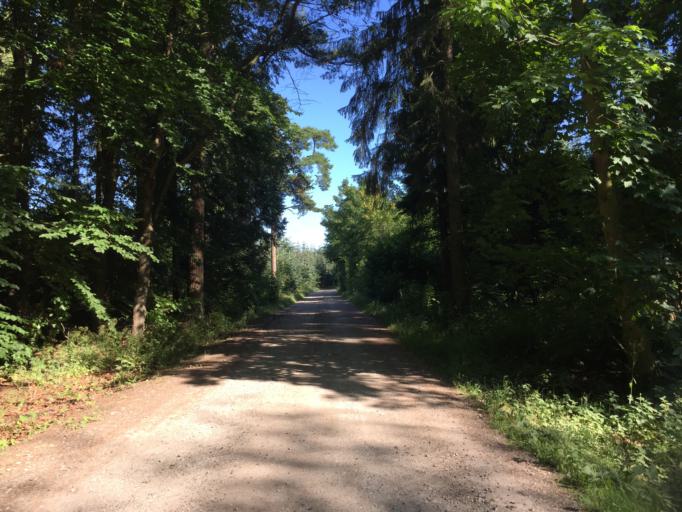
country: DK
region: South Denmark
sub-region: Kerteminde Kommune
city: Langeskov
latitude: 55.3612
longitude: 10.5511
